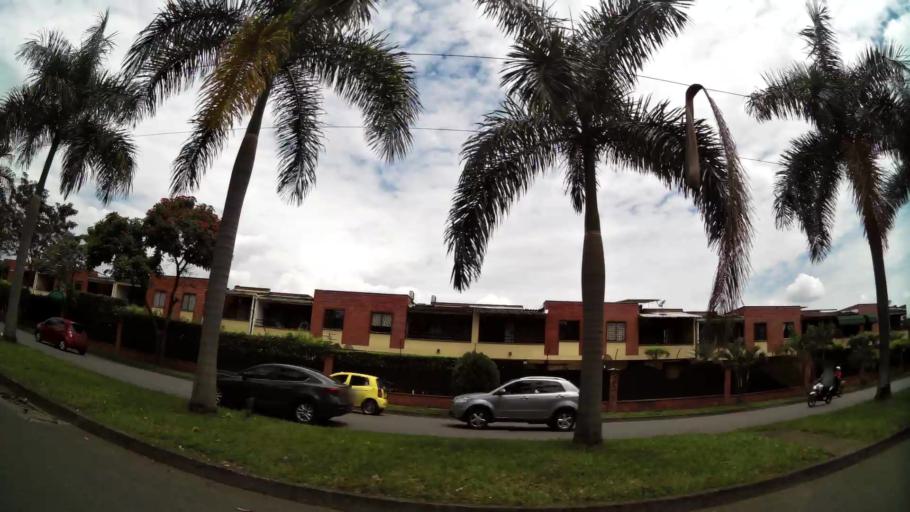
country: CO
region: Valle del Cauca
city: Cali
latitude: 3.3973
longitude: -76.5264
